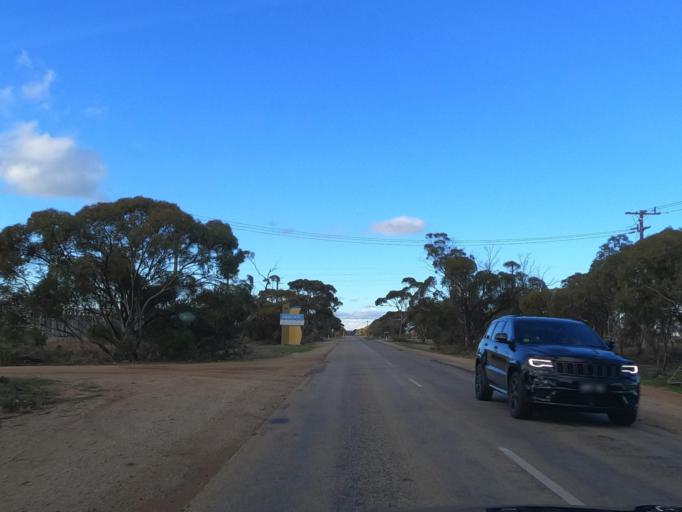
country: AU
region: Victoria
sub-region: Swan Hill
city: Swan Hill
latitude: -35.3462
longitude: 143.5219
